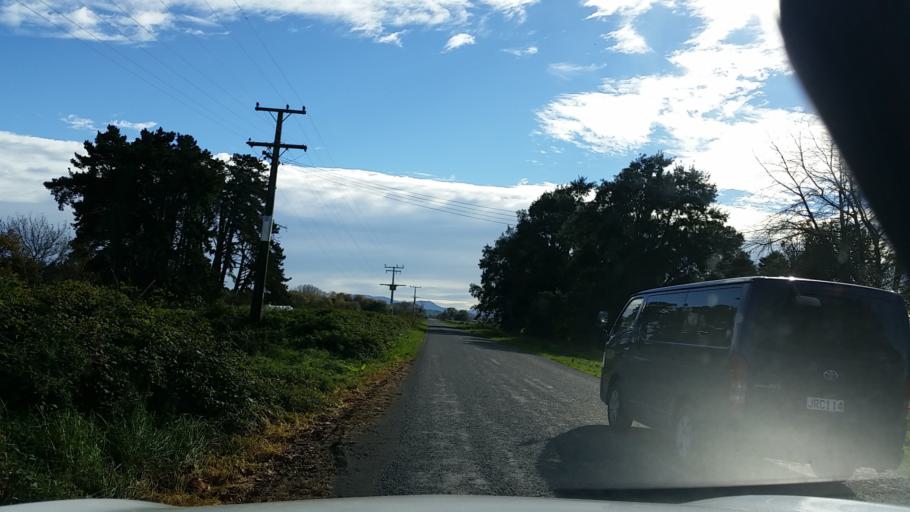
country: NZ
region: Waikato
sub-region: Hamilton City
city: Hamilton
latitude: -37.6574
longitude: 175.4363
